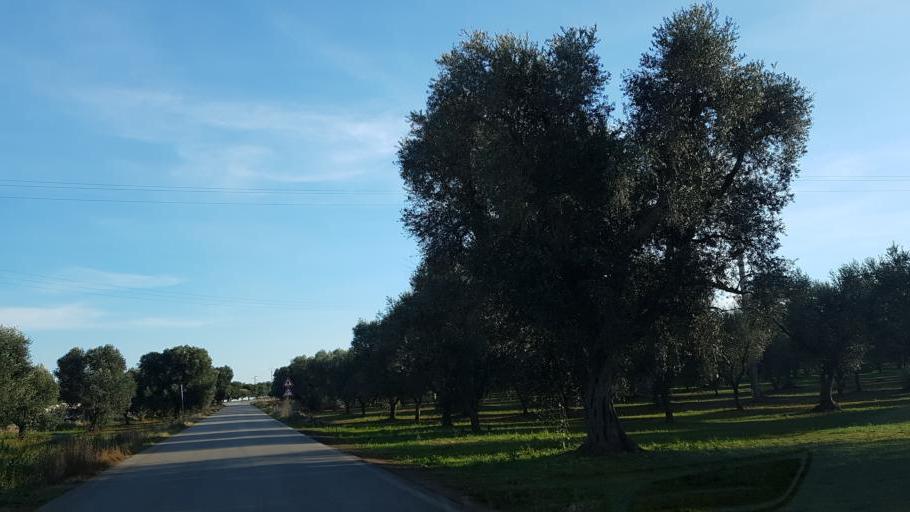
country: IT
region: Apulia
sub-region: Provincia di Brindisi
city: San Vito dei Normanni
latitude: 40.6909
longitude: 17.7627
